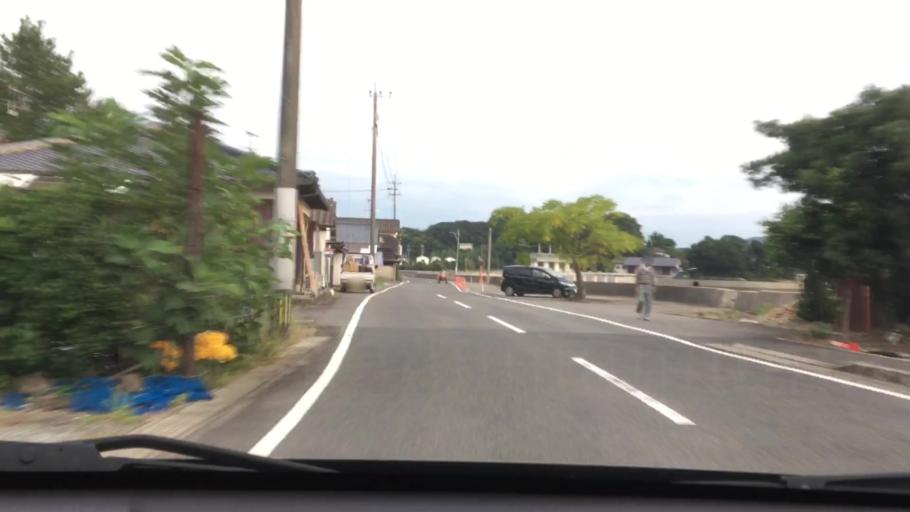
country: JP
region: Nagasaki
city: Sasebo
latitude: 33.0022
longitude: 129.7641
